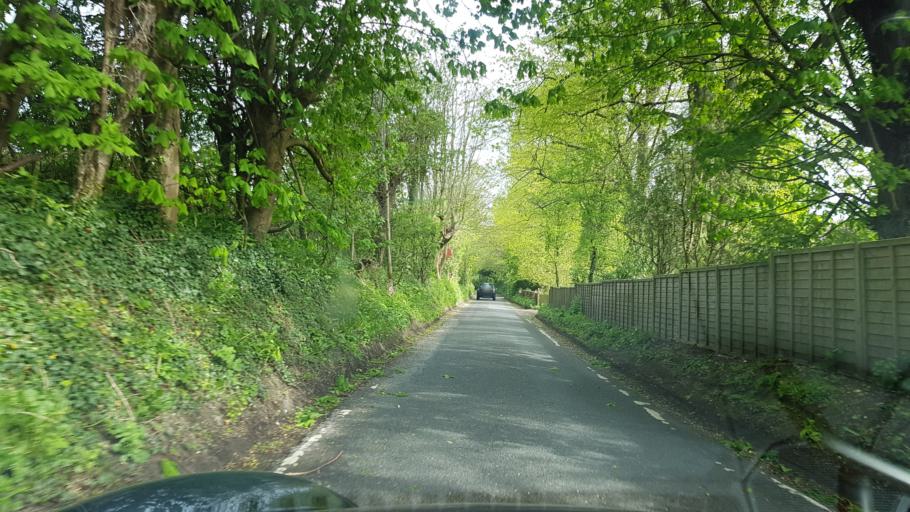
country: GB
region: England
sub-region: Hampshire
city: Kingsclere
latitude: 51.3228
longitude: -1.2524
